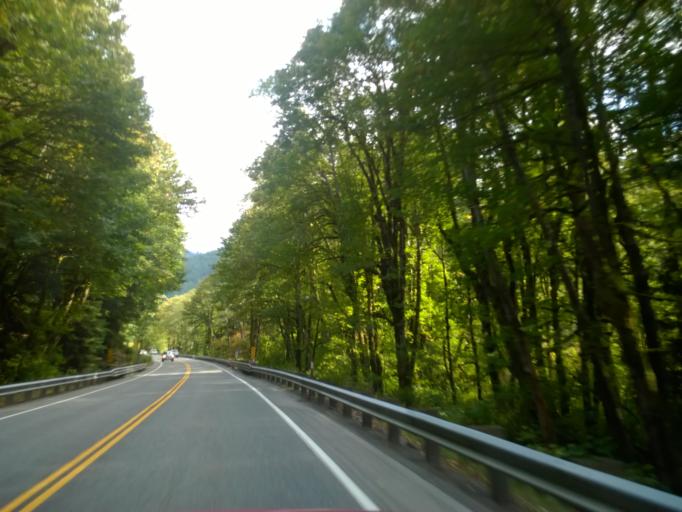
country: US
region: Washington
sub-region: Snohomish County
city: Gold Bar
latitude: 47.7135
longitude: -121.3763
